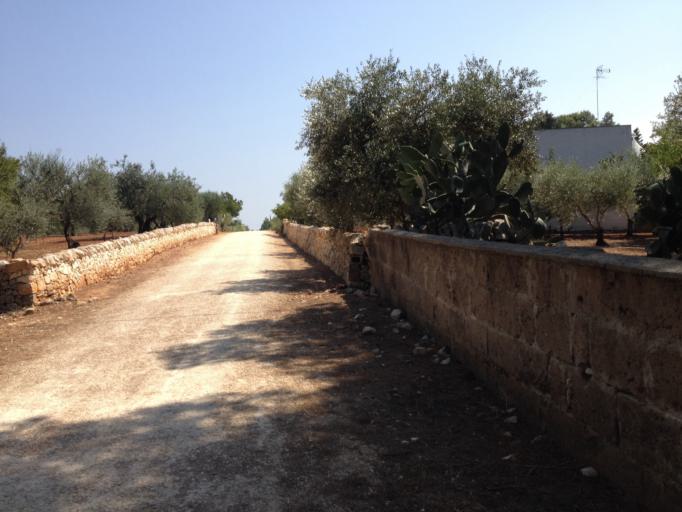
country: IT
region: Apulia
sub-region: Provincia di Brindisi
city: Cisternino
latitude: 40.7205
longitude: 17.3998
